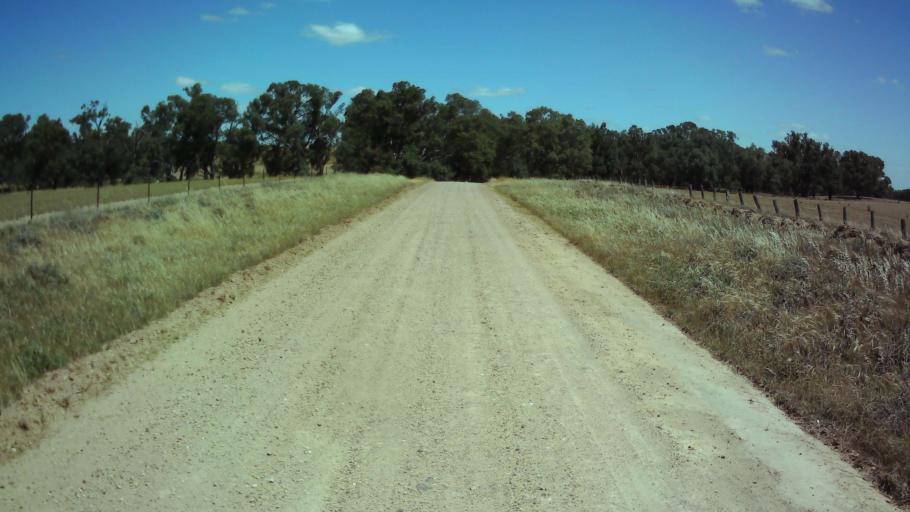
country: AU
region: New South Wales
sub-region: Weddin
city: Grenfell
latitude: -33.9314
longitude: 148.3344
